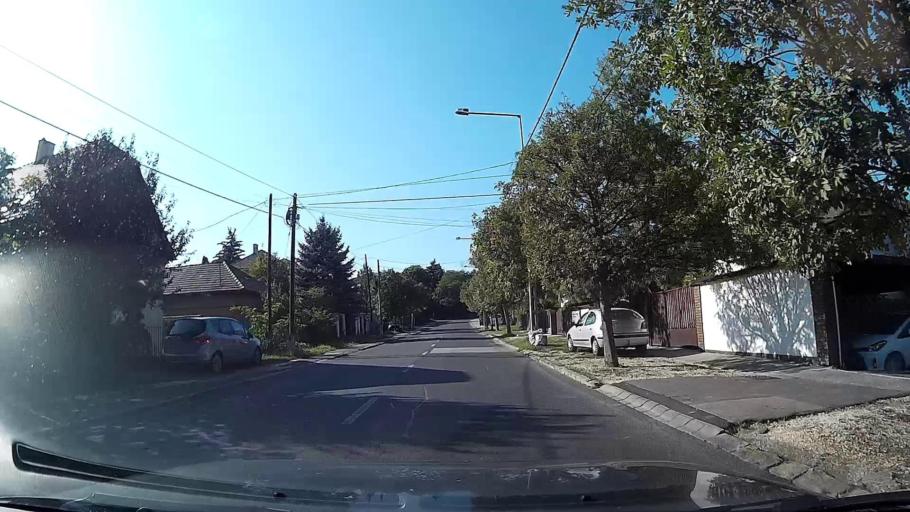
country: HU
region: Budapest
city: Budapest XXII. keruelet
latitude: 47.4115
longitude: 19.0196
